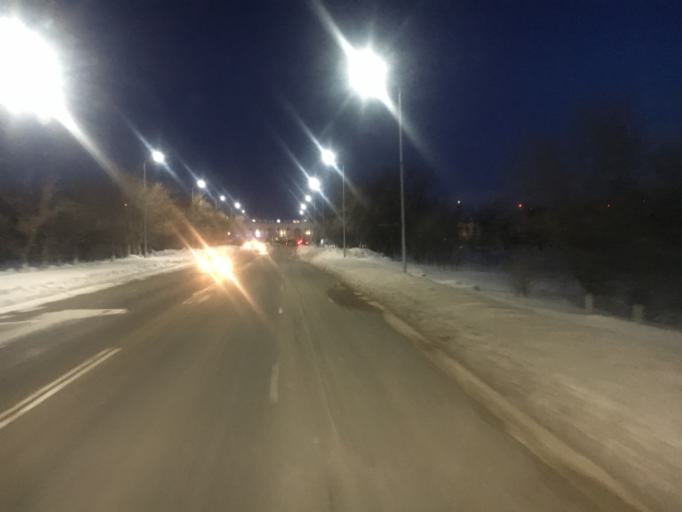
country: KZ
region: Batys Qazaqstan
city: Oral
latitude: 51.1557
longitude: 51.5358
